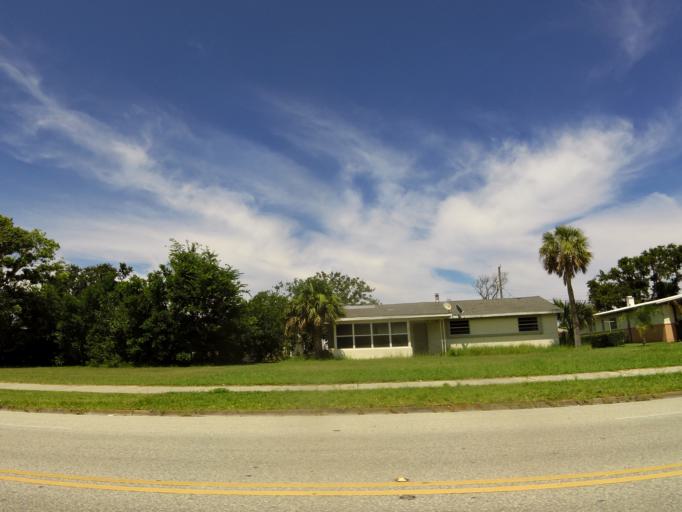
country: US
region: Florida
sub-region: Volusia County
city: Holly Hill
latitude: 29.2346
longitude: -81.0304
